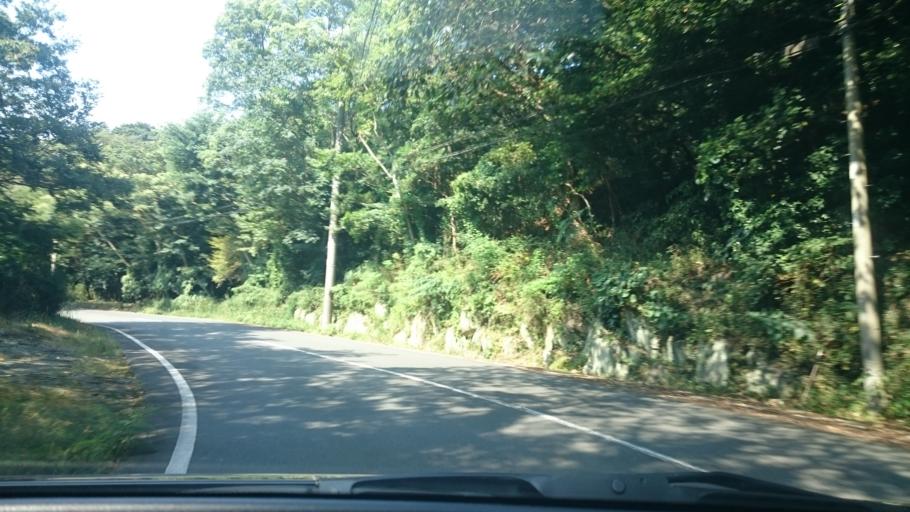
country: JP
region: Shizuoka
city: Heda
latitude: 34.9642
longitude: 138.7706
